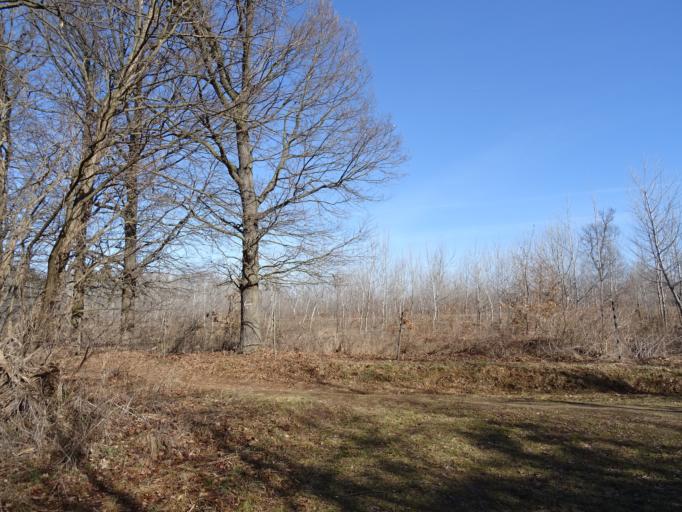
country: HU
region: Pest
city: Szada
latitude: 47.6019
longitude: 19.3064
